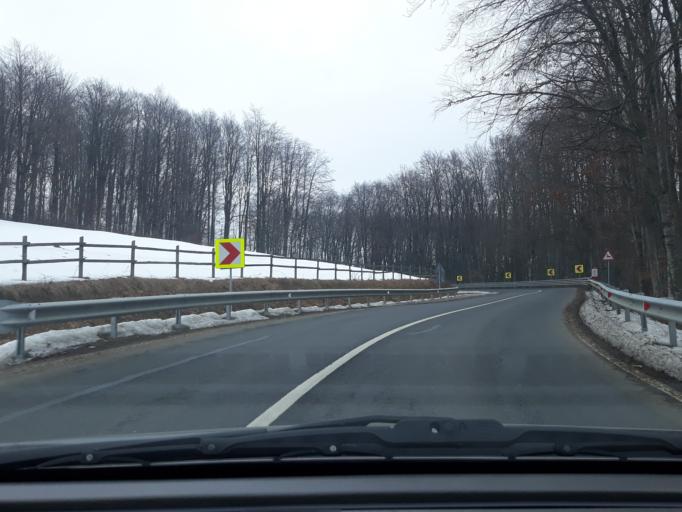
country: RO
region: Bihor
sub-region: Comuna Sinteu
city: Sinteu
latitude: 47.1222
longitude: 22.4567
